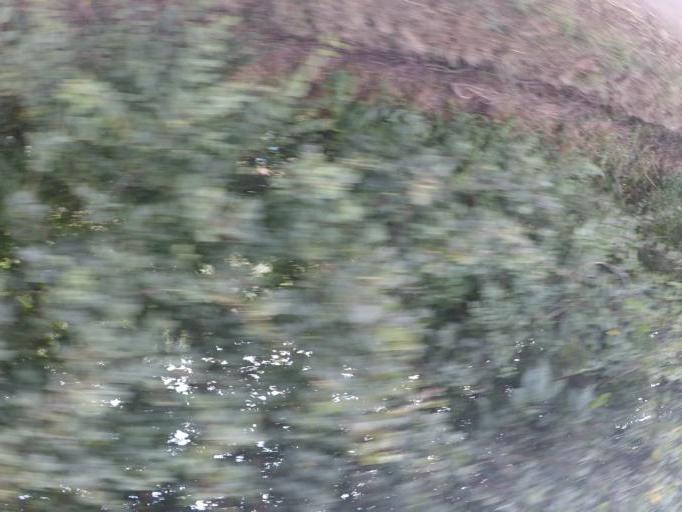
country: FR
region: Brittany
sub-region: Departement des Cotes-d'Armor
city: Plelo
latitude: 48.5590
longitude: -2.9522
